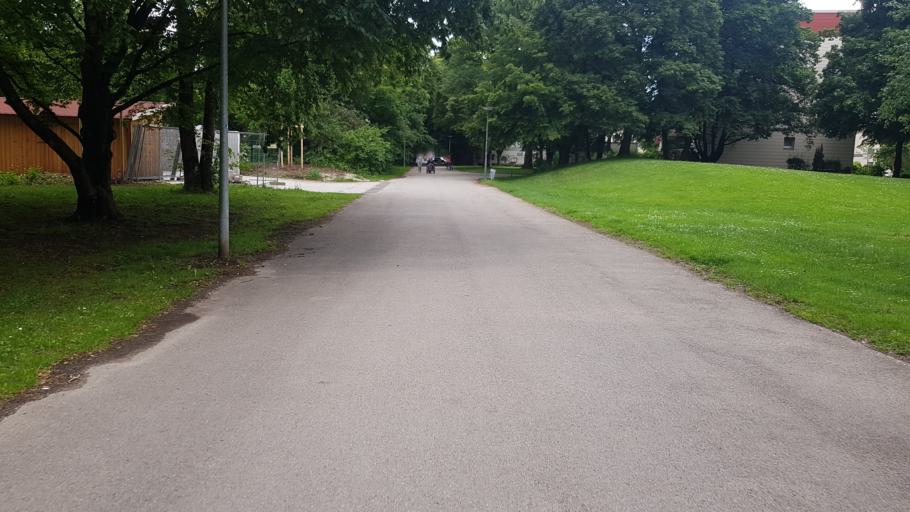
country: DE
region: Bavaria
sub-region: Upper Bavaria
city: Pasing
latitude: 48.1476
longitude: 11.4367
